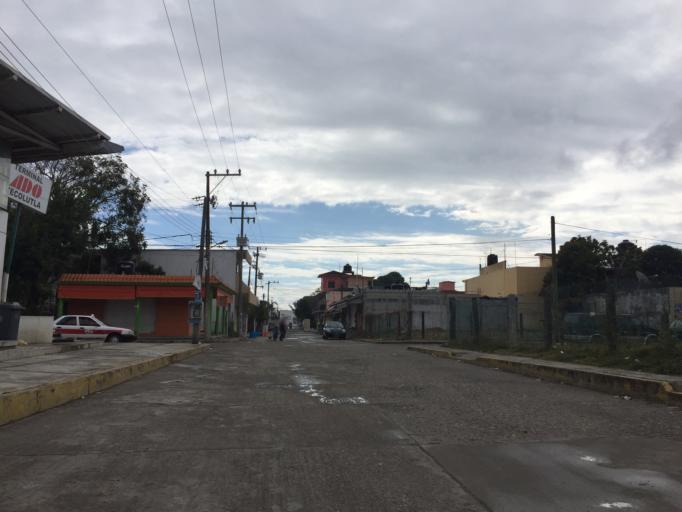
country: MX
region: Veracruz
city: Tecolutla
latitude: 20.4788
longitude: -97.0092
